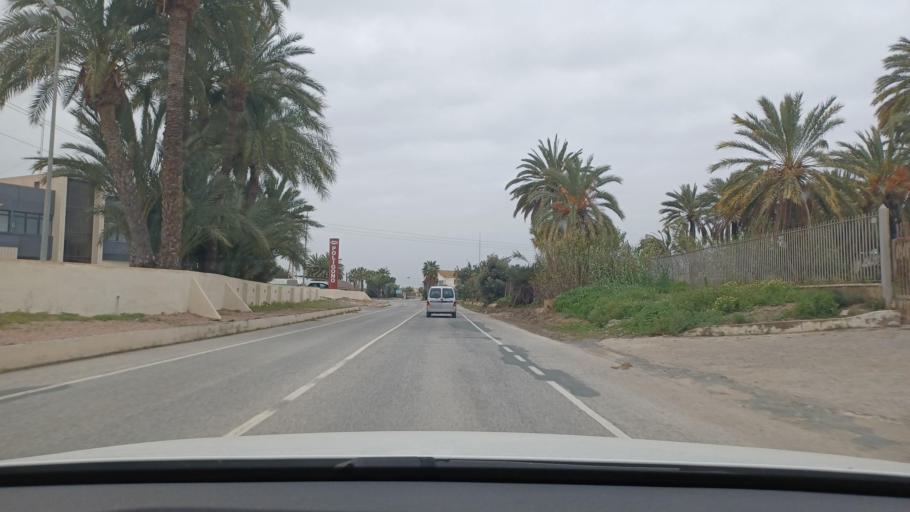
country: ES
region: Valencia
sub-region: Provincia de Alicante
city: Elche
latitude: 38.2413
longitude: -0.7096
